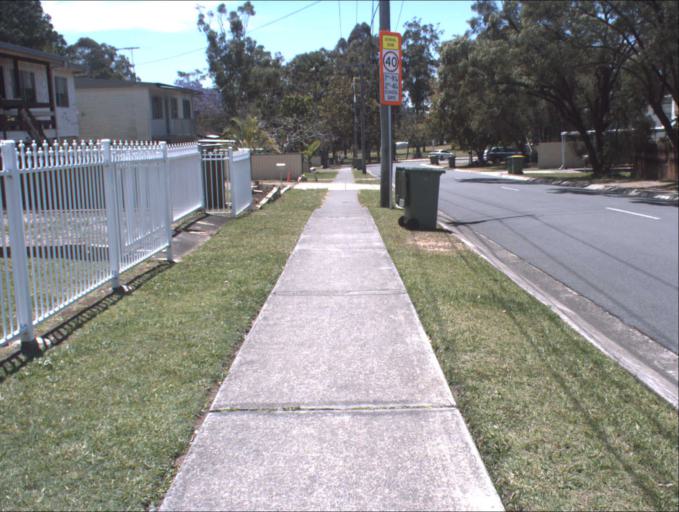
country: AU
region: Queensland
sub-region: Logan
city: Woodridge
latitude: -27.6280
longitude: 153.1045
